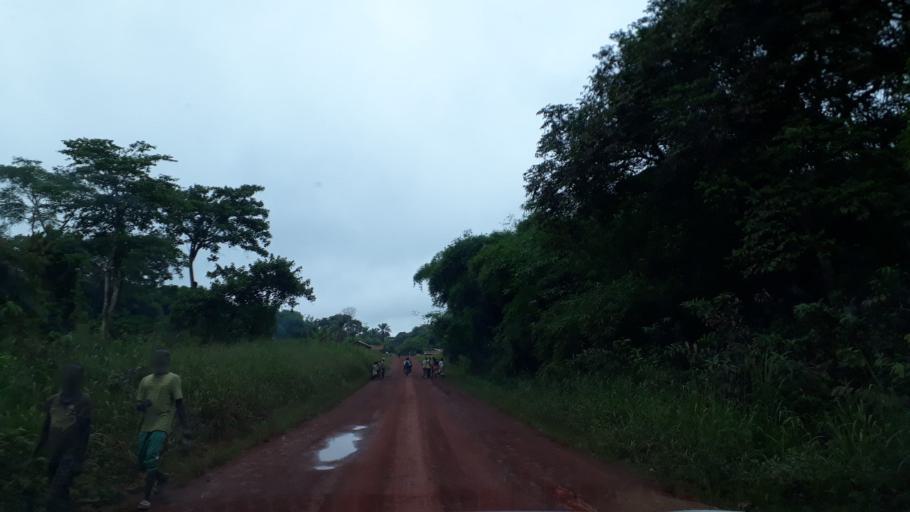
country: CD
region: Eastern Province
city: Wamba
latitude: 1.3634
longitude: 27.5945
